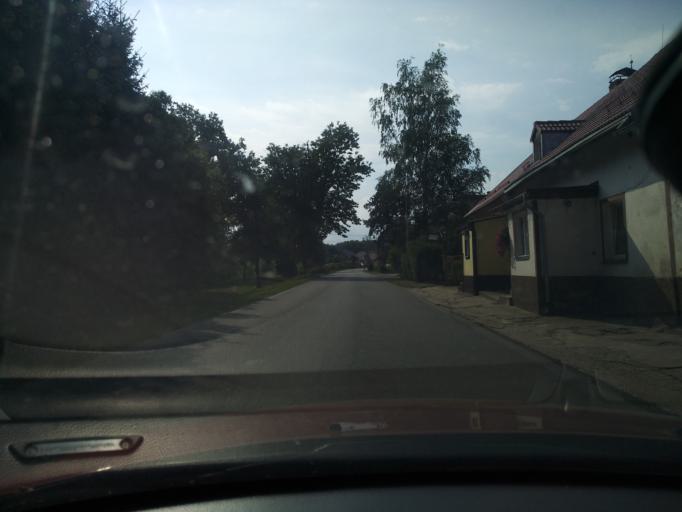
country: PL
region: Lower Silesian Voivodeship
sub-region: Powiat jeleniogorski
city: Stara Kamienica
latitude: 50.9209
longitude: 15.5718
